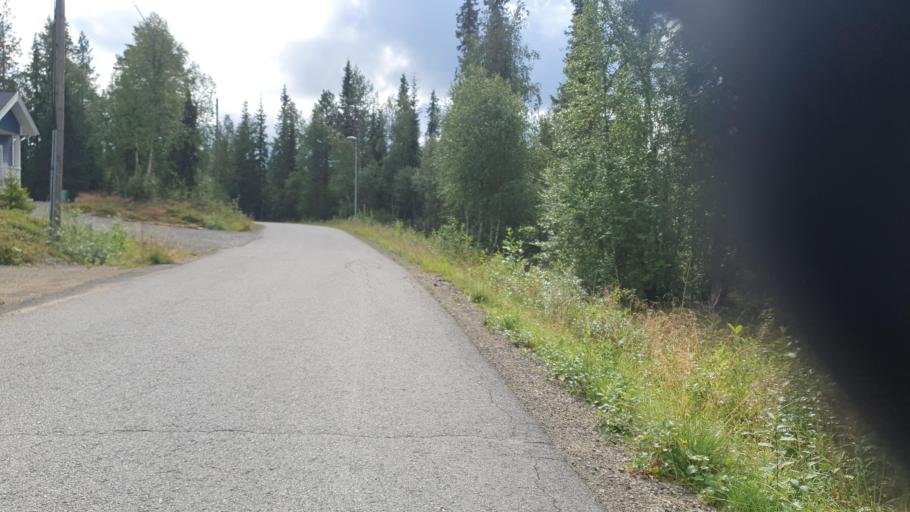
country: FI
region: Lapland
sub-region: Tunturi-Lappi
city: Kolari
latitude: 67.6206
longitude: 24.1465
